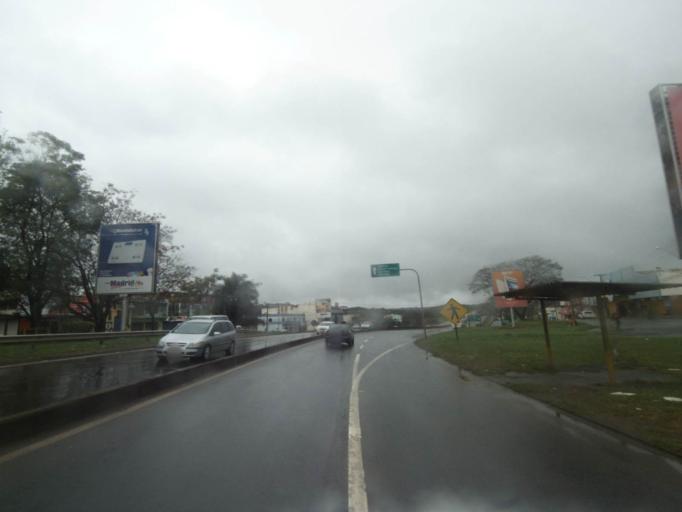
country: PY
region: Alto Parana
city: Ciudad del Este
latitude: -25.5061
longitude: -54.5890
